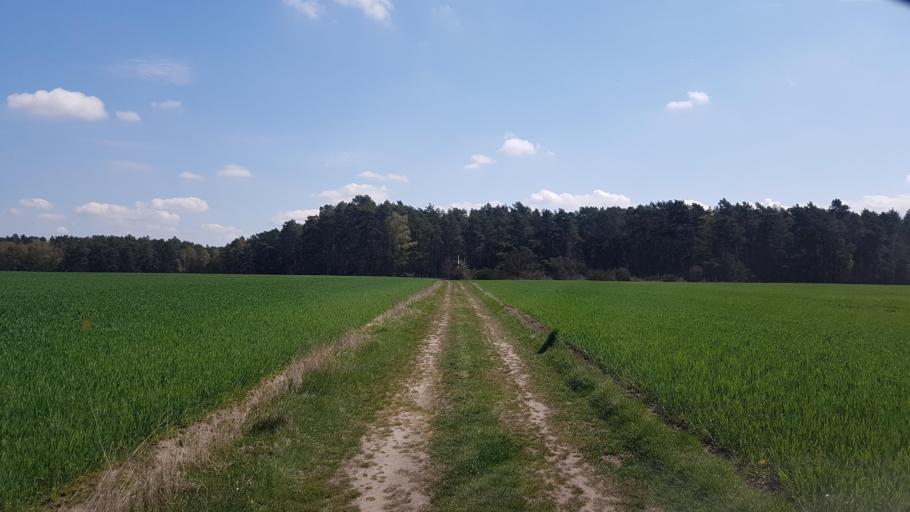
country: DE
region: Brandenburg
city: Bronkow
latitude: 51.6729
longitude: 13.9252
